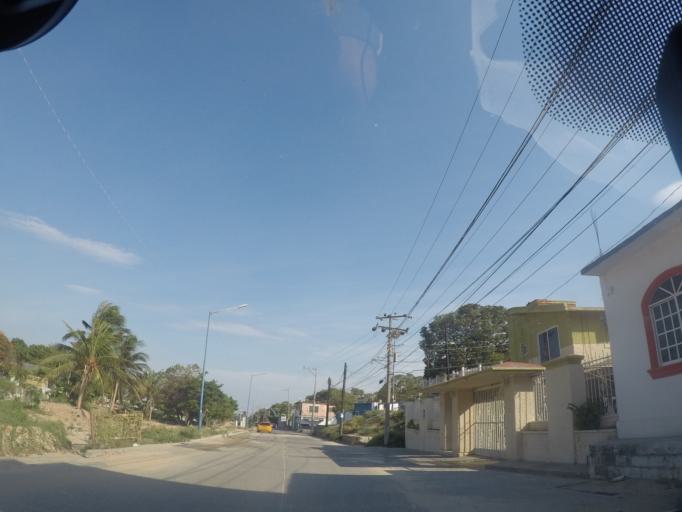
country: MX
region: Oaxaca
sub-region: Salina Cruz
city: Salina Cruz
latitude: 16.1887
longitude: -95.2021
